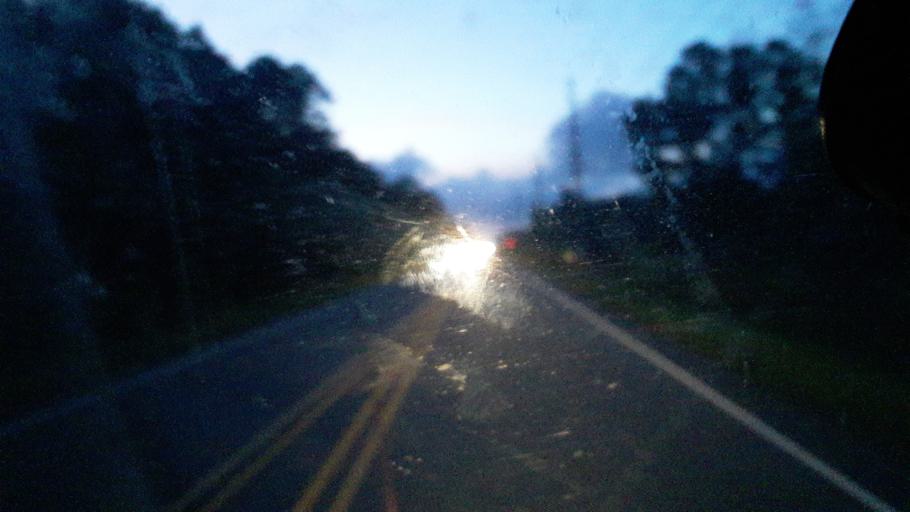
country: US
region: North Carolina
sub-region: Brunswick County
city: Oak Island
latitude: 33.9918
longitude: -78.2133
